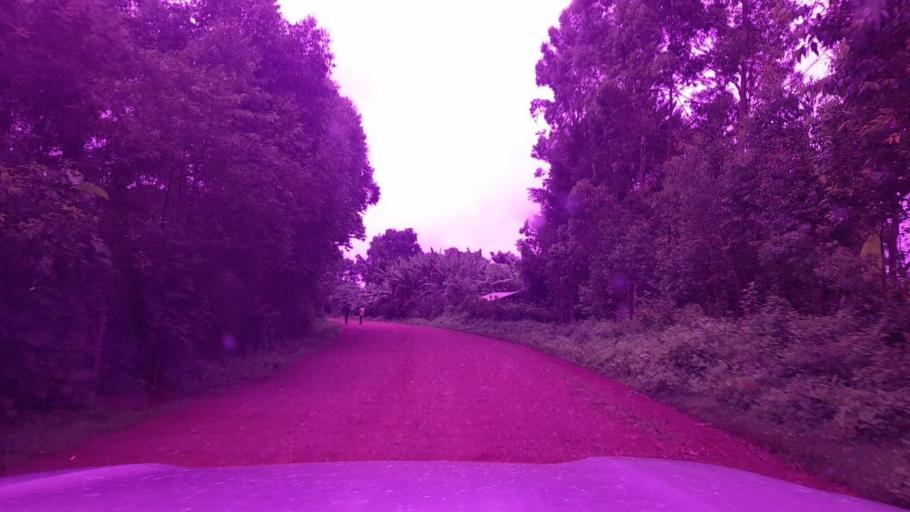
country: ET
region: Southern Nations, Nationalities, and People's Region
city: Bonga
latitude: 7.5799
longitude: 36.0335
